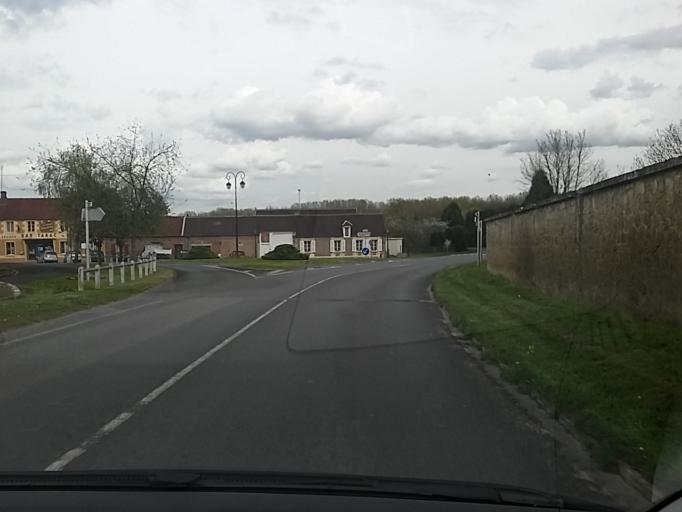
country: FR
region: Picardie
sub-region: Departement de l'Oise
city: Longueil-Sainte-Marie
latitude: 49.3476
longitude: 2.7312
